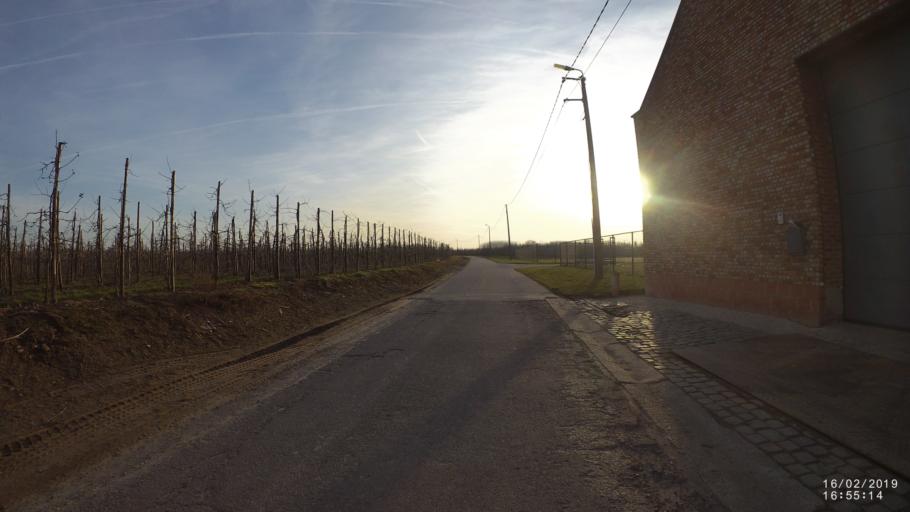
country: BE
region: Flanders
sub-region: Provincie Vlaams-Brabant
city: Zoutleeuw
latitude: 50.8217
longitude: 5.1337
